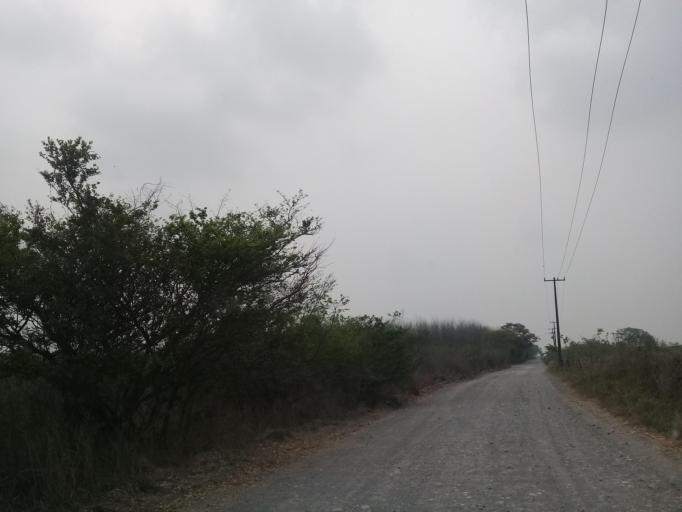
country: MX
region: Veracruz
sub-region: Medellin
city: La Laguna y Monte del Castillo
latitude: 18.9042
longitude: -96.1793
